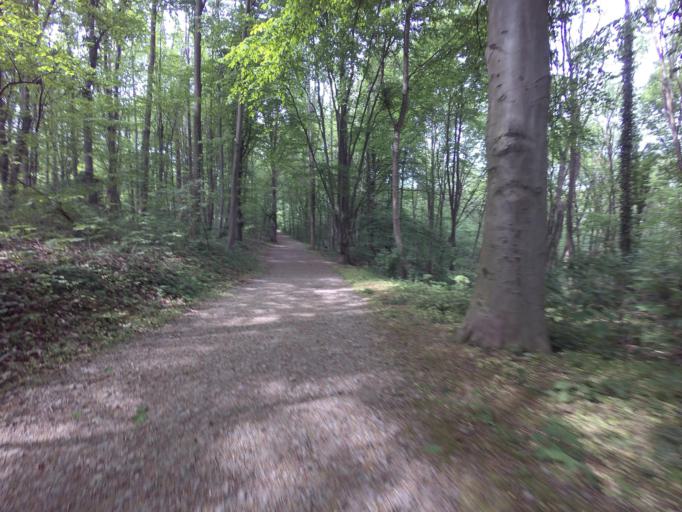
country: DE
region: Lower Saxony
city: Nordstemmen
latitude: 52.1730
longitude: 9.7674
